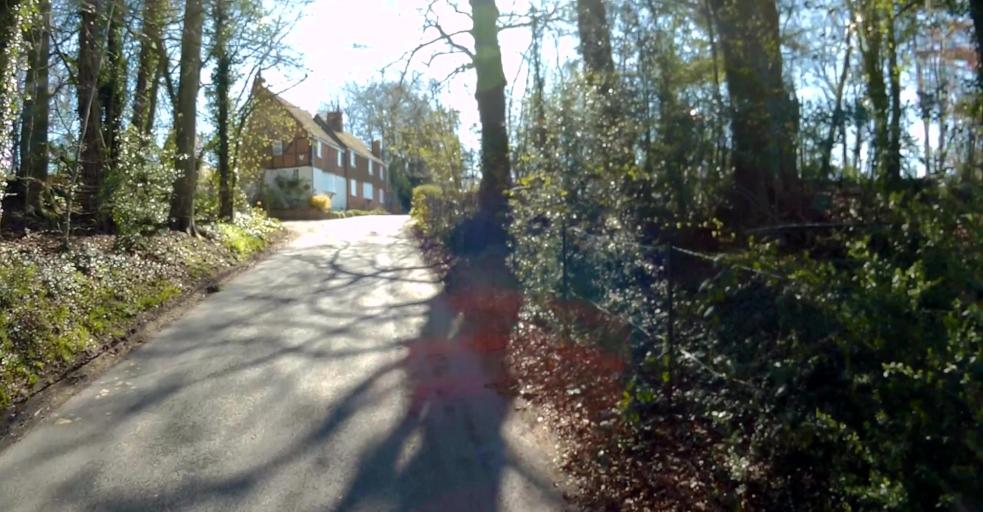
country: GB
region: England
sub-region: Surrey
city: Farnham
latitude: 51.2136
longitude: -0.8341
